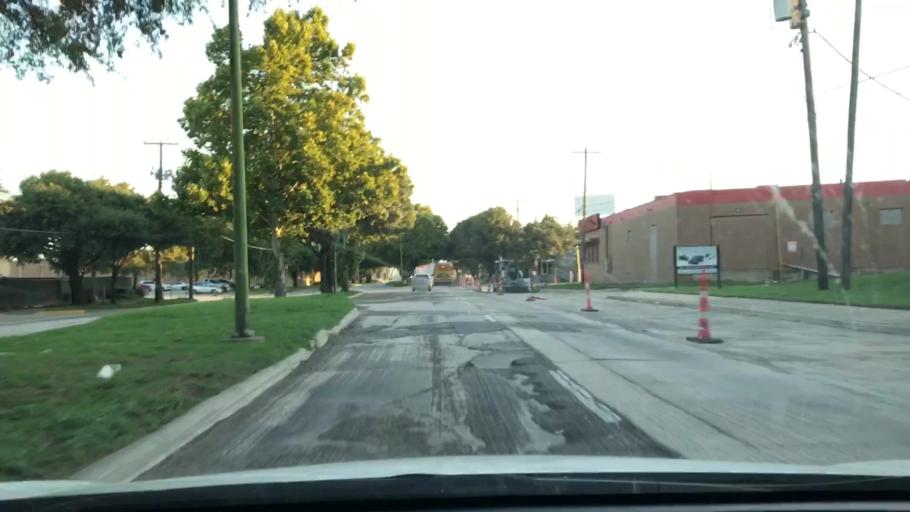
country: US
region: Texas
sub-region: Dallas County
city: Dallas
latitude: 32.7997
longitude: -96.8331
